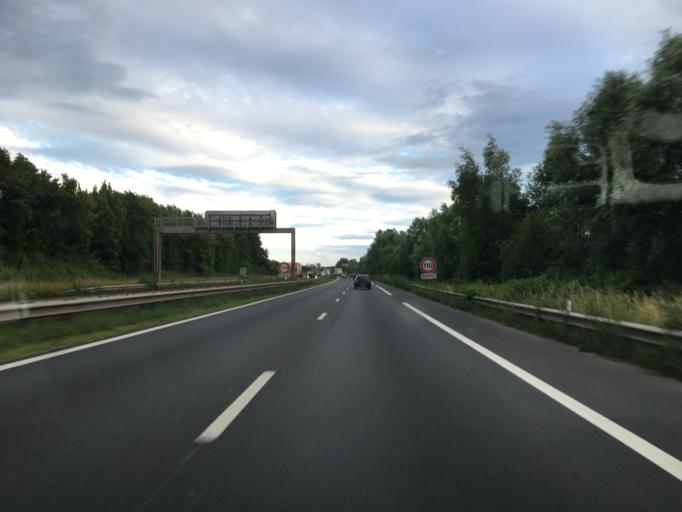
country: FR
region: Ile-de-France
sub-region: Departement de Seine-et-Marne
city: Brie-Comte-Robert
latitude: 48.6916
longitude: 2.5952
